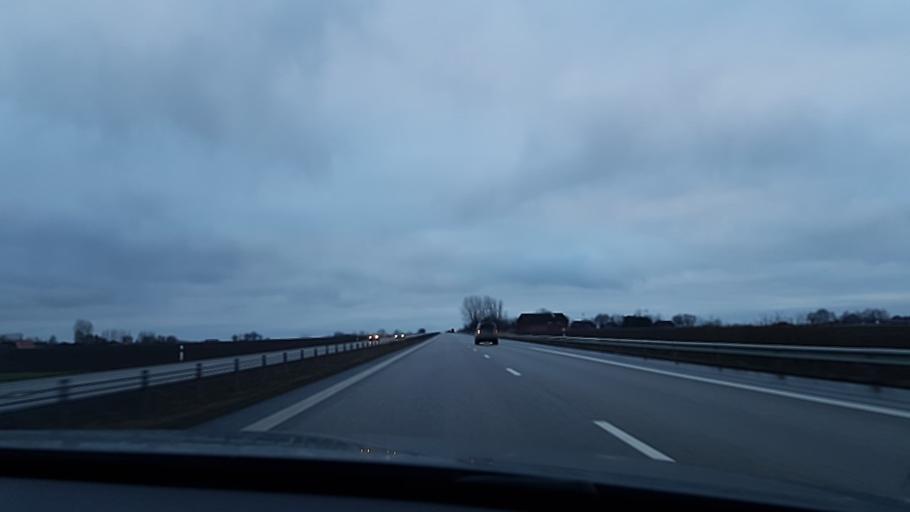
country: SE
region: Skane
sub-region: Astorps Kommun
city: Astorp
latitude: 56.1764
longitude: 13.0013
